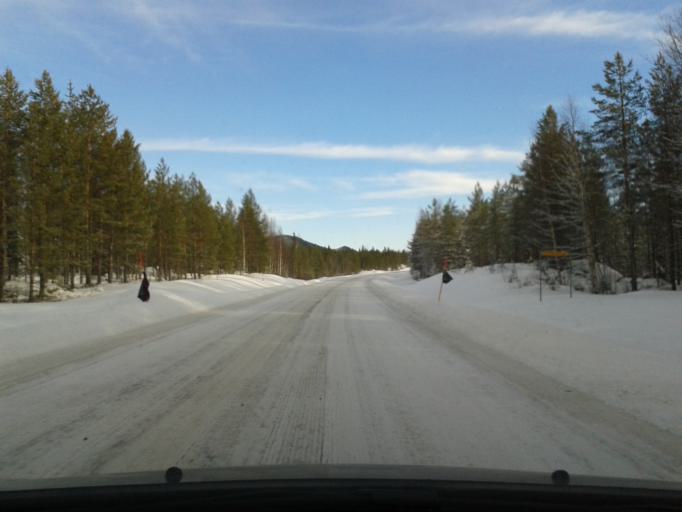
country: SE
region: Vaesterbotten
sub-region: Asele Kommun
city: Asele
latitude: 64.3166
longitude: 17.1578
